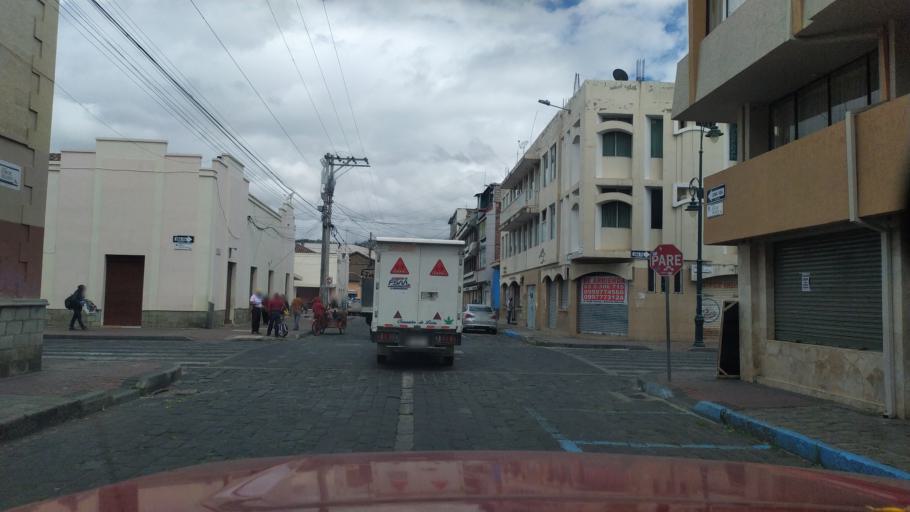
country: EC
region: Chimborazo
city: Riobamba
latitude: -1.6741
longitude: -78.6470
